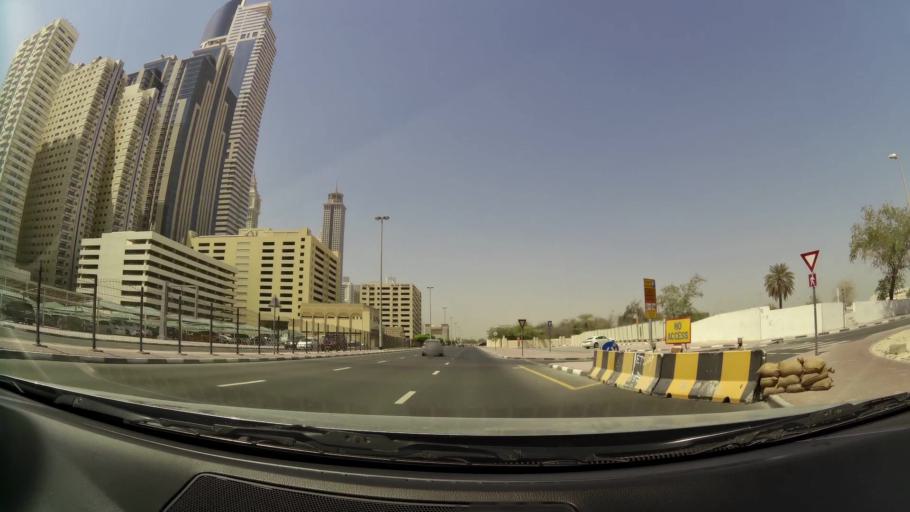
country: AE
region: Ash Shariqah
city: Sharjah
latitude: 25.2242
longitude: 55.2806
